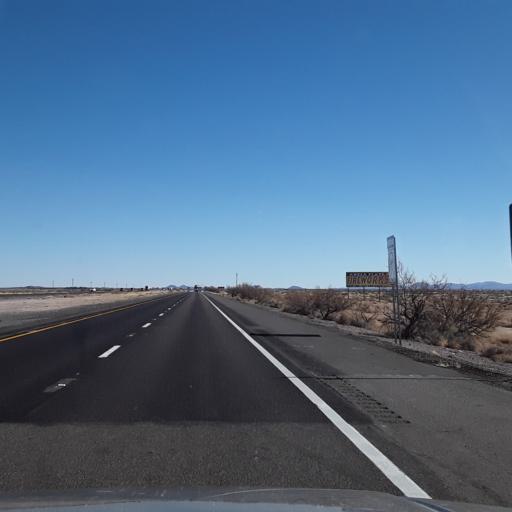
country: US
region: New Mexico
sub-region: Luna County
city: Deming
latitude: 32.2495
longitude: -107.4657
